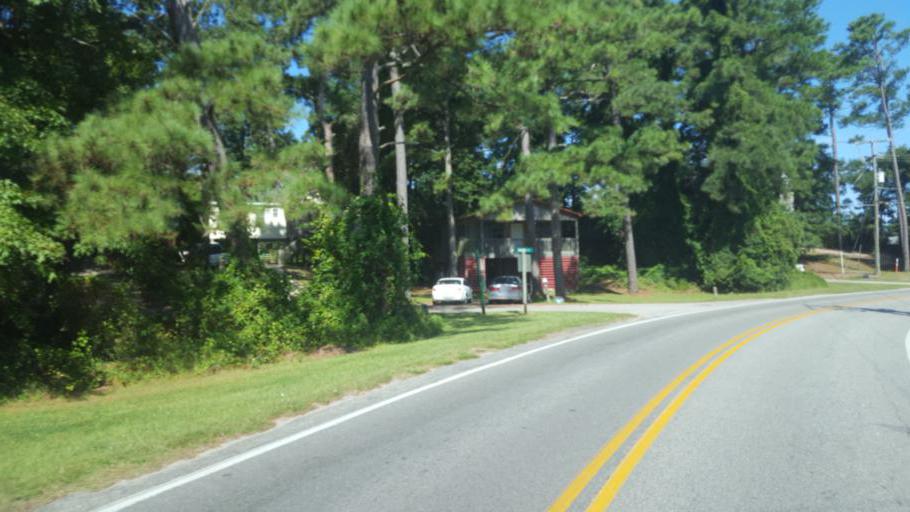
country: US
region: North Carolina
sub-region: Dare County
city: Kill Devil Hills
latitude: 36.0122
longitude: -75.7116
